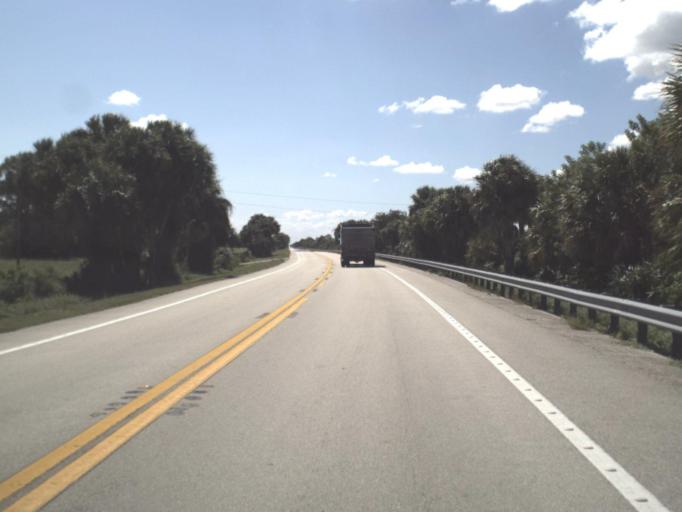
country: US
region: Florida
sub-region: Glades County
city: Buckhead Ridge
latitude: 27.1066
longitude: -80.9450
